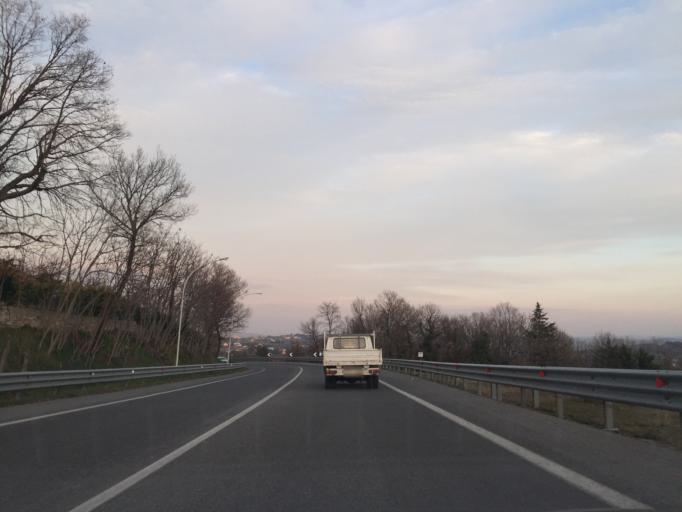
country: IT
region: Molise
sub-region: Provincia di Campobasso
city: Campobasso
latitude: 41.5604
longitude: 14.6903
